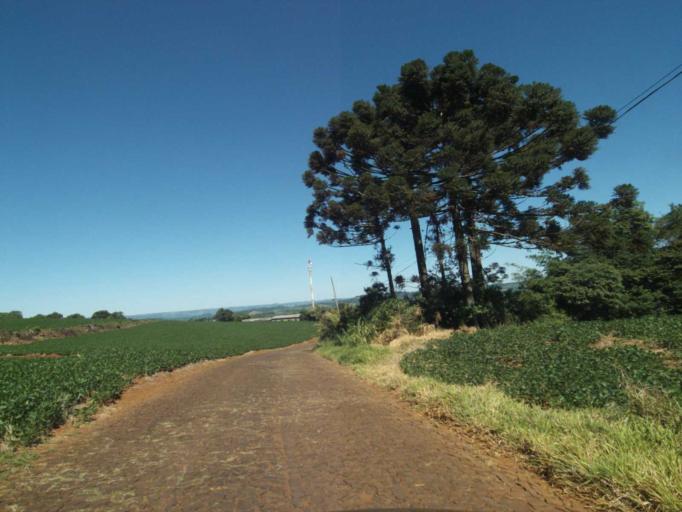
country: BR
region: Parana
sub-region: Coronel Vivida
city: Coronel Vivida
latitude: -25.9593
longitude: -52.8236
